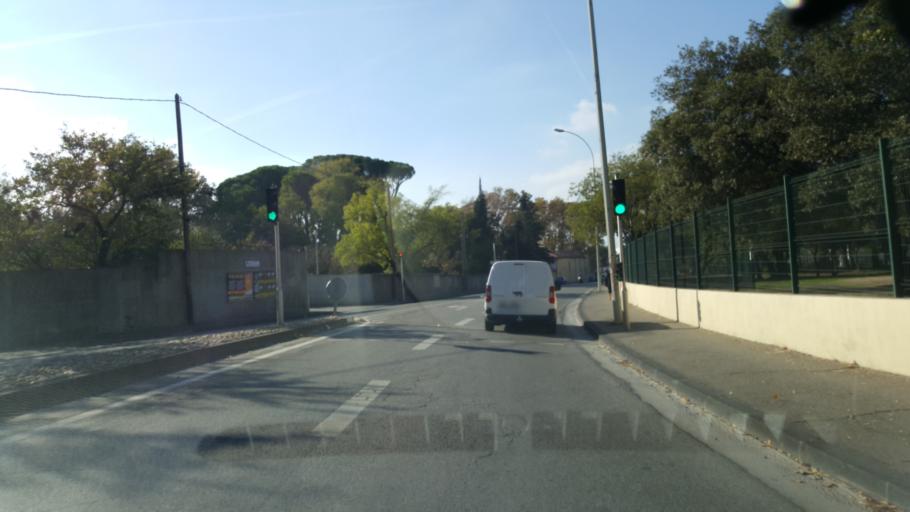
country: FR
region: Provence-Alpes-Cote d'Azur
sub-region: Departement des Bouches-du-Rhone
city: Marseille 10
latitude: 43.2681
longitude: 5.4182
